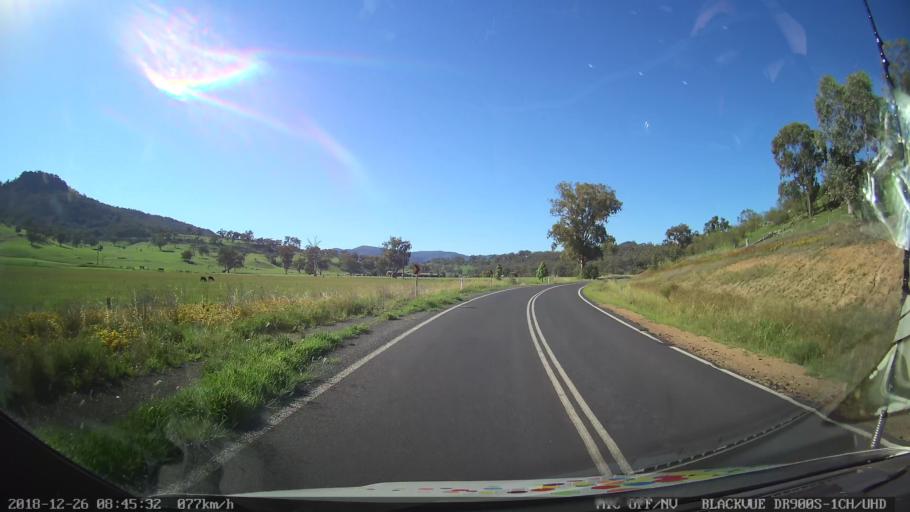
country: AU
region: New South Wales
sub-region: Mid-Western Regional
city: Kandos
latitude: -32.5261
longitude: 150.0870
